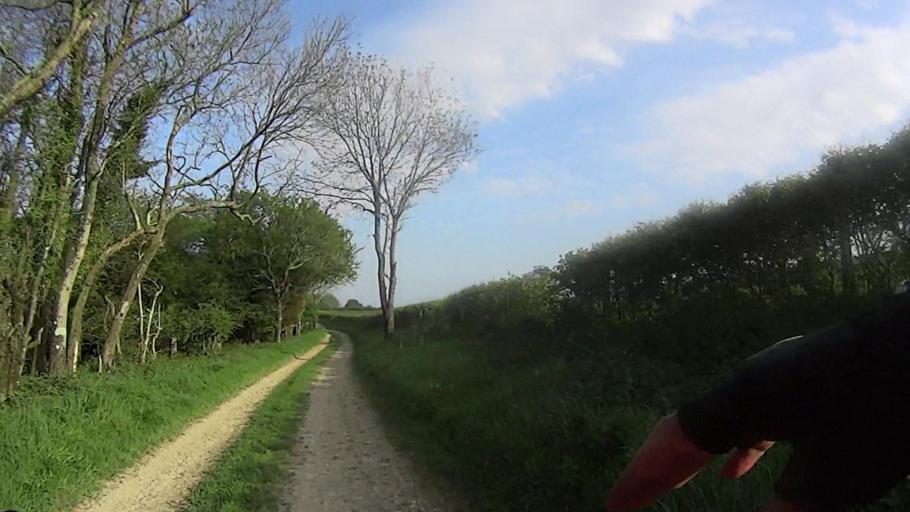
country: GB
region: England
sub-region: West Sussex
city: Fontwell
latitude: 50.9092
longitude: -0.6366
